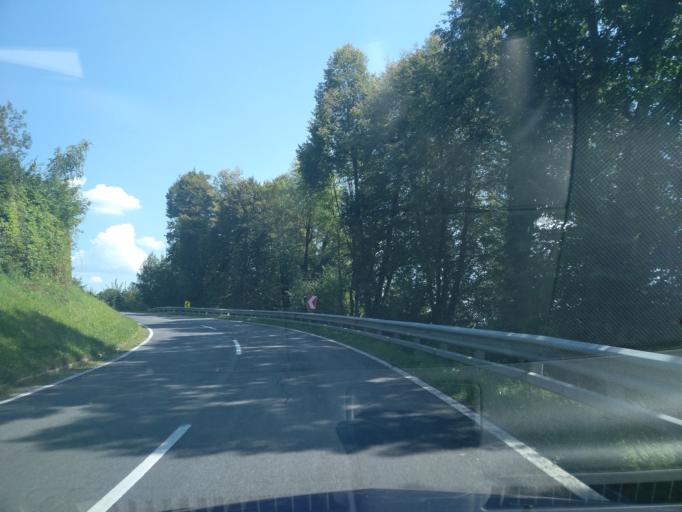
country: AT
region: Styria
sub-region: Politischer Bezirk Leibnitz
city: Leutschach
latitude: 46.6713
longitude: 15.4727
